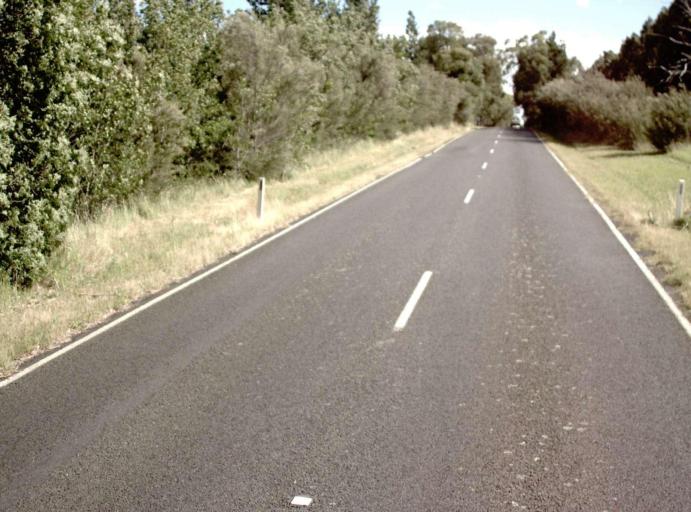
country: AU
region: Victoria
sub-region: Latrobe
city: Morwell
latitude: -38.2029
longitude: 146.4013
